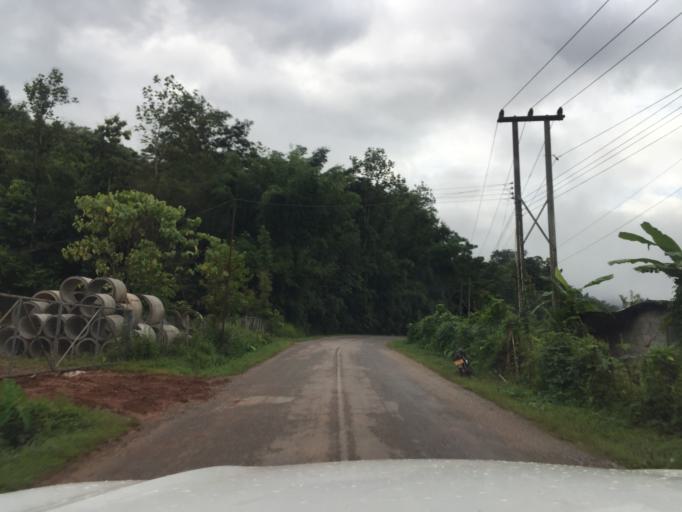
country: LA
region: Oudomxai
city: Muang La
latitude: 20.8476
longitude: 102.1058
